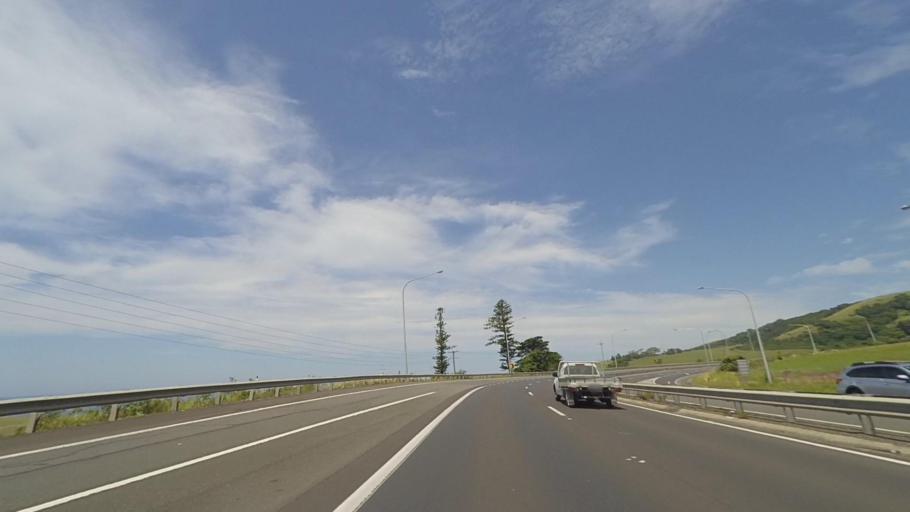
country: AU
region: New South Wales
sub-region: Kiama
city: Kiama
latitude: -34.6971
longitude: 150.8435
